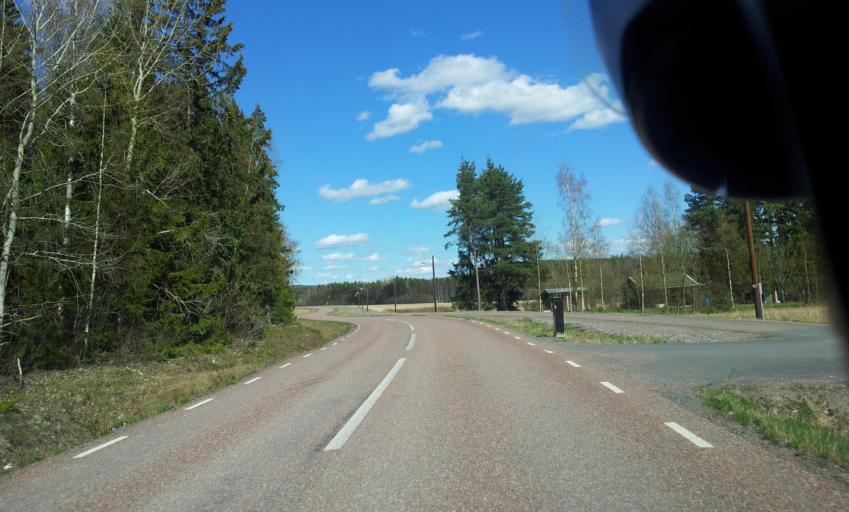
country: SE
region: Dalarna
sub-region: Borlange Kommun
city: Ornas
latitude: 60.4955
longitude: 15.5398
